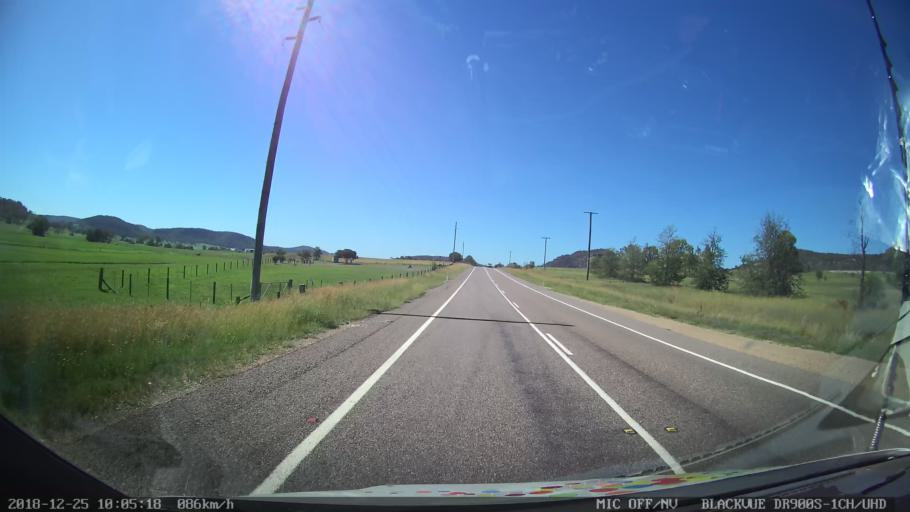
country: AU
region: New South Wales
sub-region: Upper Hunter Shire
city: Merriwa
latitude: -32.2454
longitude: 150.4859
